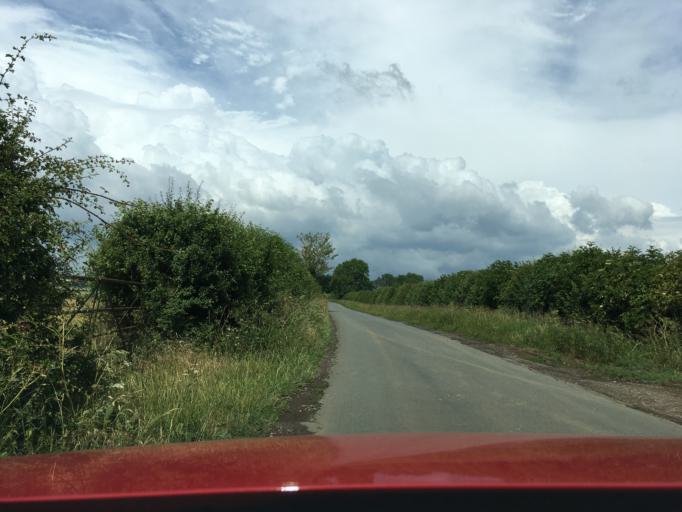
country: GB
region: England
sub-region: Gloucestershire
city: Chalford
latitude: 51.6896
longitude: -2.1298
